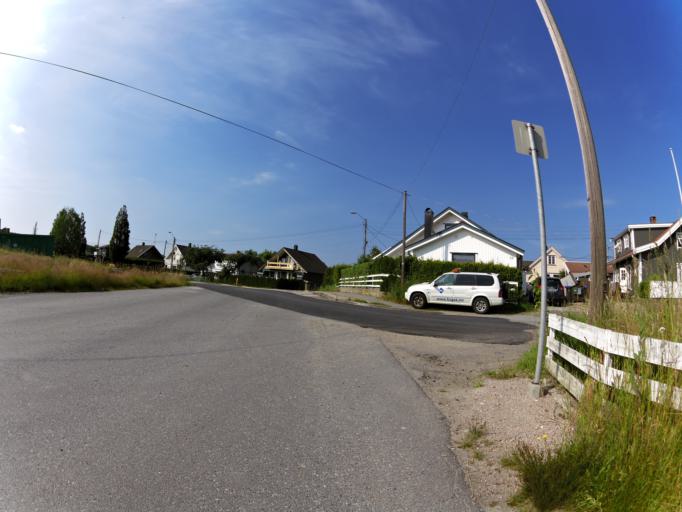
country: NO
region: Ostfold
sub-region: Fredrikstad
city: Fredrikstad
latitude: 59.2323
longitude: 10.9838
